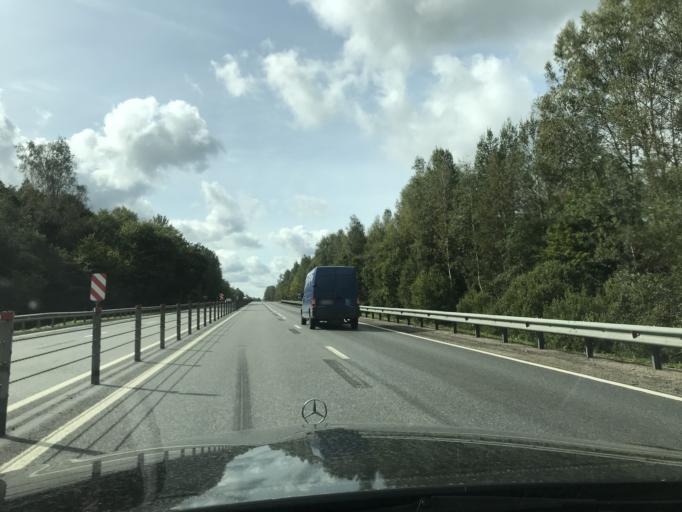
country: RU
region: Smolensk
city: Pechersk
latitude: 54.9495
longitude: 32.1927
